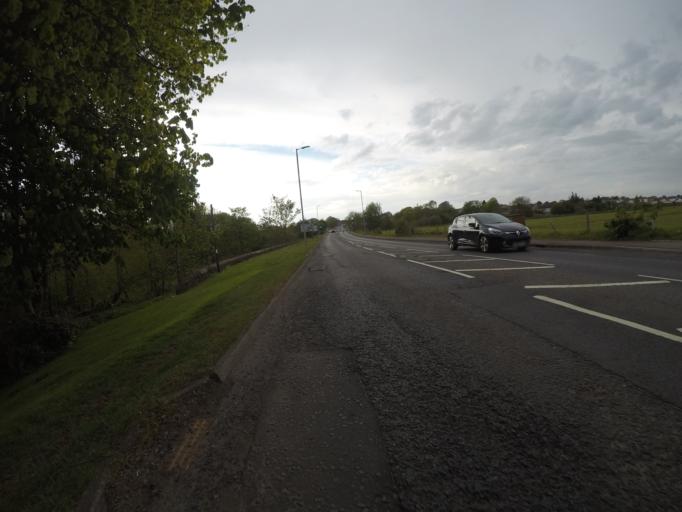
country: GB
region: Scotland
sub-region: North Ayrshire
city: Irvine
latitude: 55.6105
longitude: -4.6511
